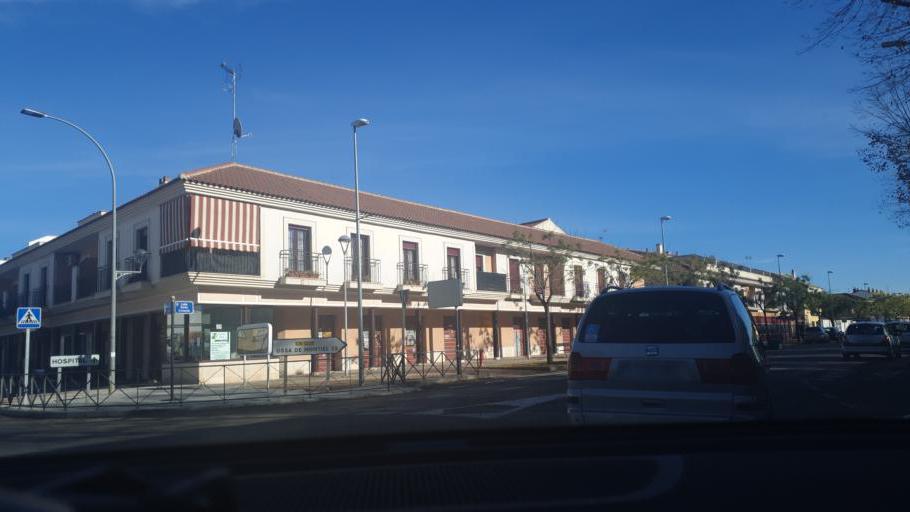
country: ES
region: Castille-La Mancha
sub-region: Provincia de Ciudad Real
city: Tomelloso
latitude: 39.1526
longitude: -3.0118
